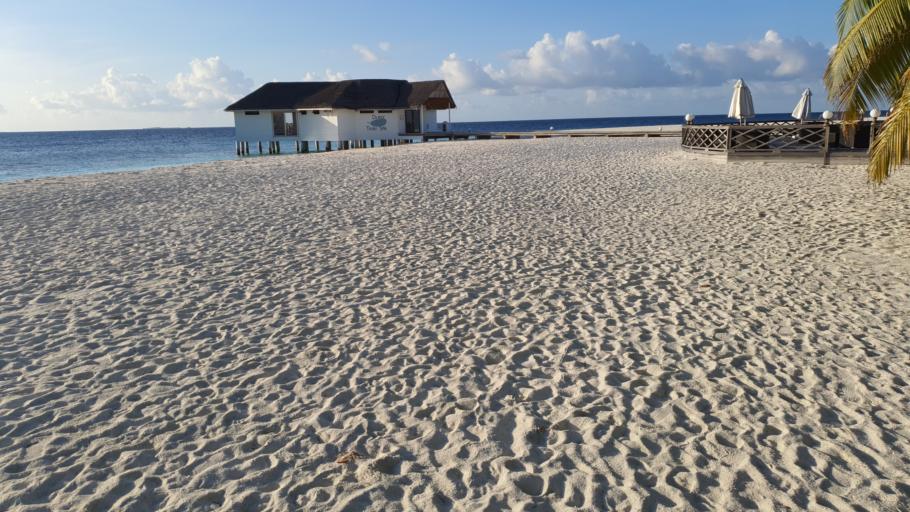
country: MV
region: North Central
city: Mahibadhoo
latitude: 3.6523
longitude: 72.8227
